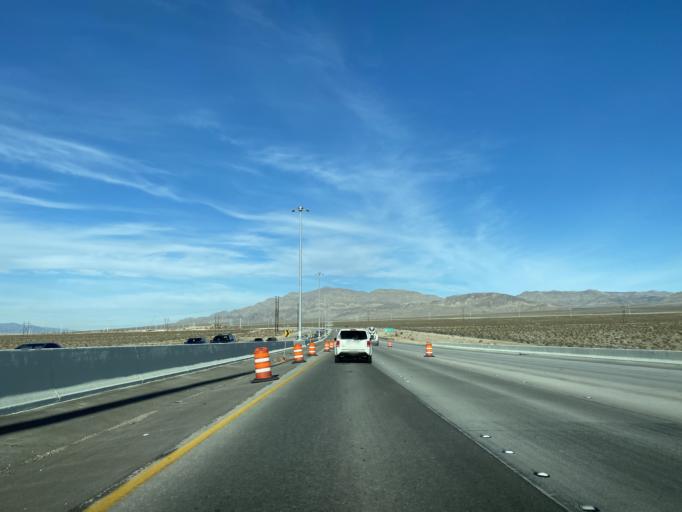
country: US
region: Nevada
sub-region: Clark County
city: Nellis Air Force Base
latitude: 36.2822
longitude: -115.0655
